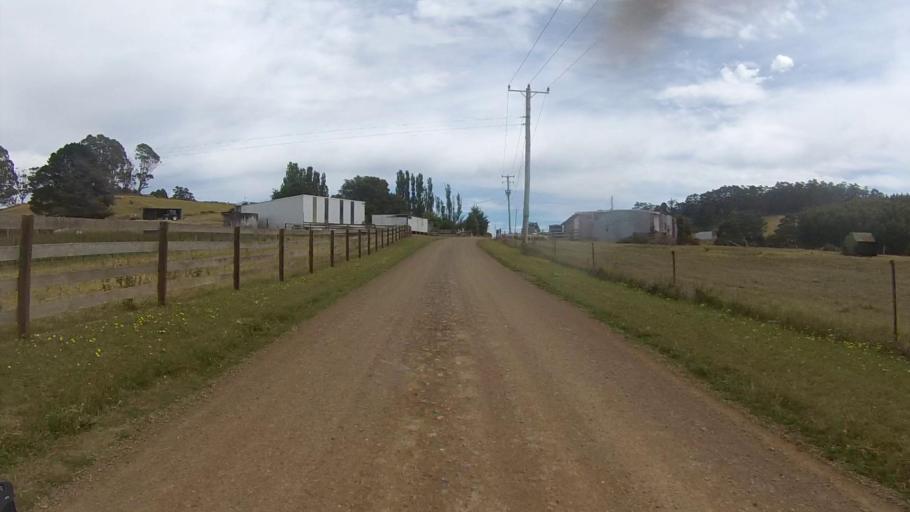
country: AU
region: Tasmania
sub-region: Sorell
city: Sorell
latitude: -42.7267
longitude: 147.7544
